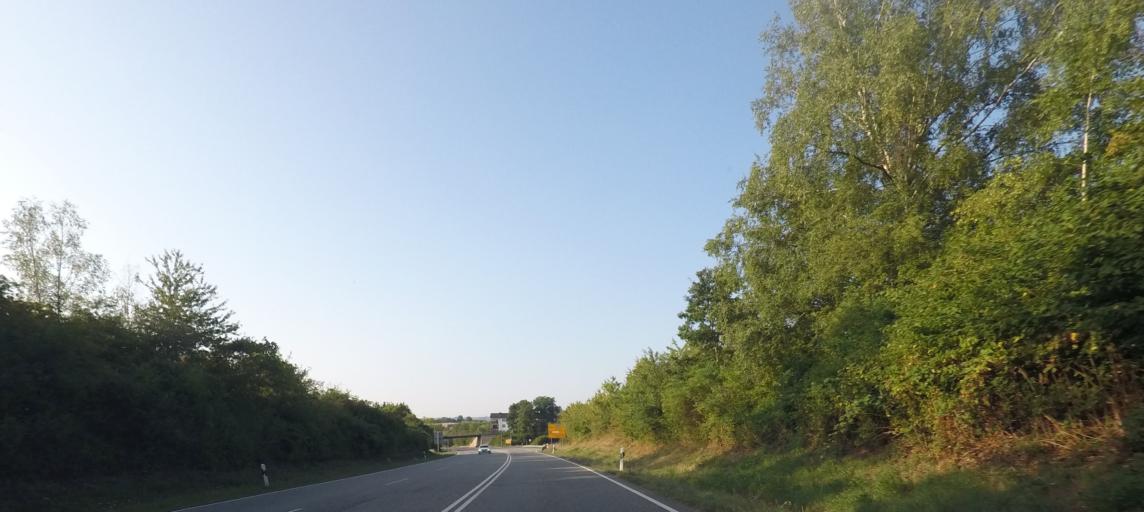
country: DE
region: Saarland
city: Heusweiler
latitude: 49.3671
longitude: 6.9245
